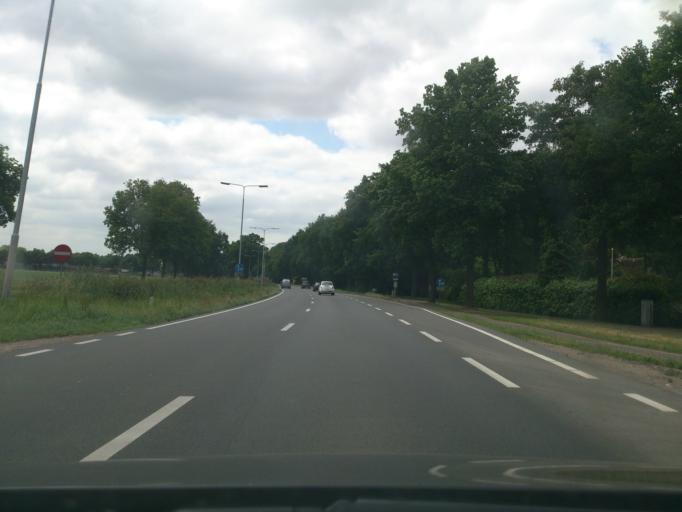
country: NL
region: North Brabant
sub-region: Gemeente Vught
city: Vught
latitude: 51.6398
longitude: 5.2513
